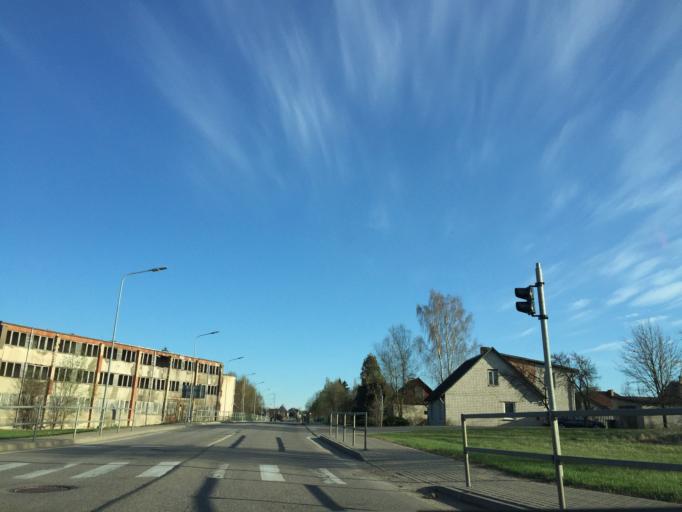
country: LV
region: Valkas Rajons
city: Valka
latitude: 57.7802
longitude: 25.9916
